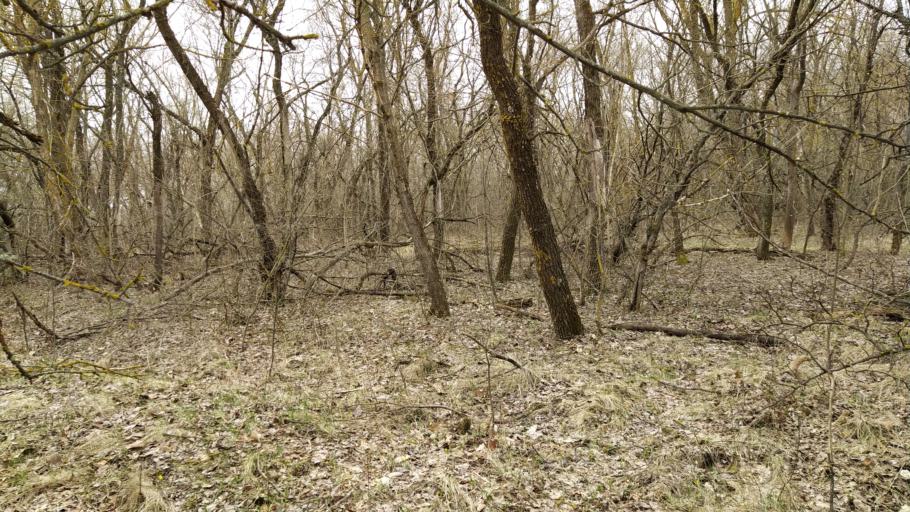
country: RU
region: Rostov
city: Semikarakorsk
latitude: 47.5390
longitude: 40.6813
